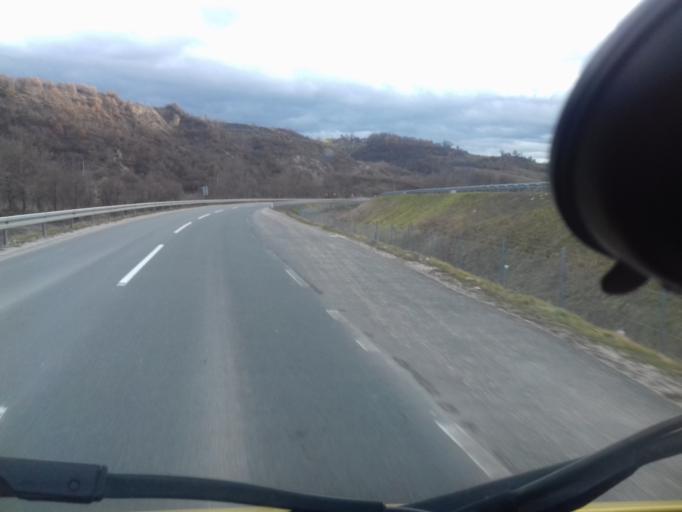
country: BA
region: Federation of Bosnia and Herzegovina
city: Kakanj
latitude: 44.1356
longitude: 18.0757
